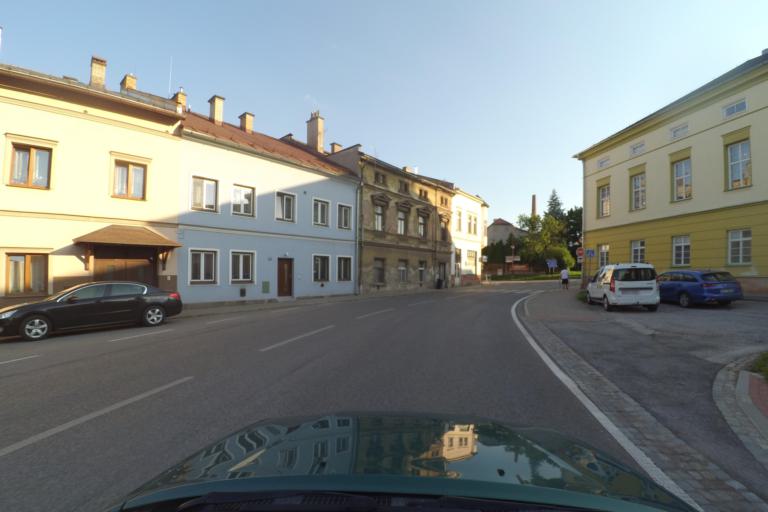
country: CZ
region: Kralovehradecky
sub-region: Okres Trutnov
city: Hostinne
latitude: 50.5426
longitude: 15.7244
